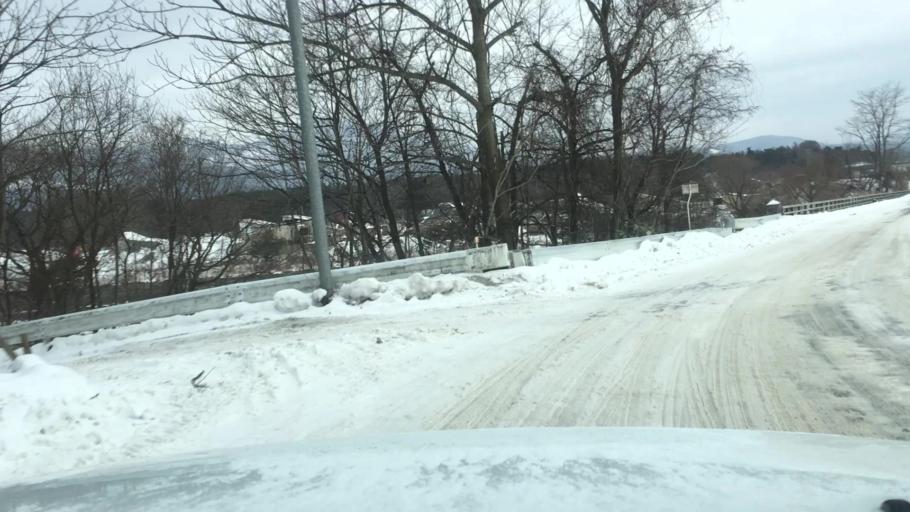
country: JP
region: Iwate
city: Shizukuishi
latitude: 39.9115
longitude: 141.0048
